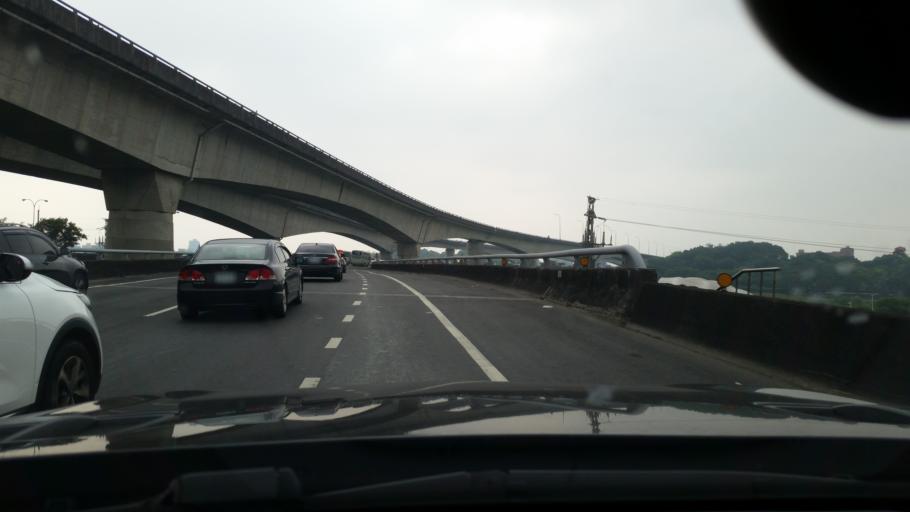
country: TW
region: Taipei
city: Taipei
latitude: 25.0740
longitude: 121.5316
